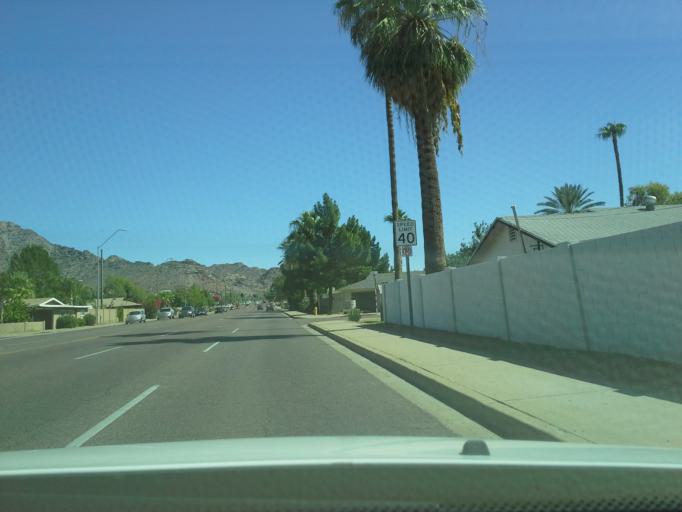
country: US
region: Arizona
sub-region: Maricopa County
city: Phoenix
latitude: 33.5381
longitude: -112.0509
